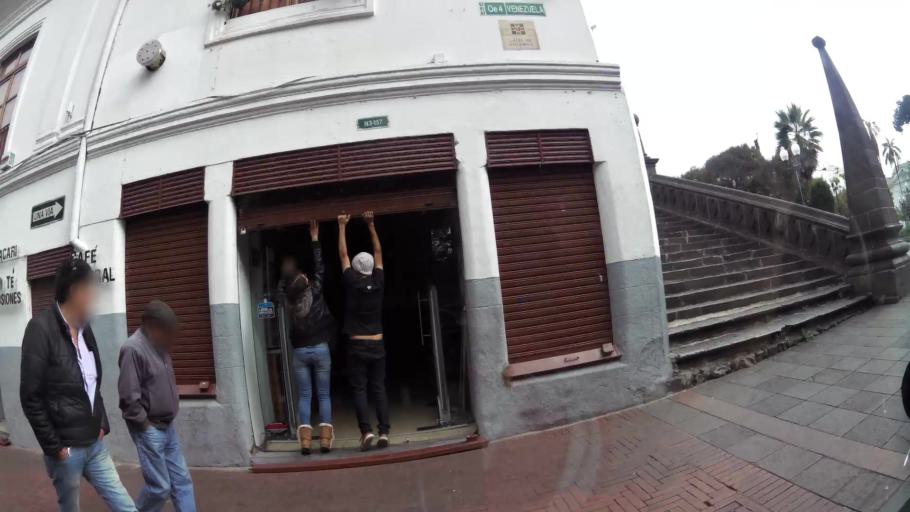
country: EC
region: Pichincha
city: Quito
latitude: -0.2207
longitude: -78.5120
